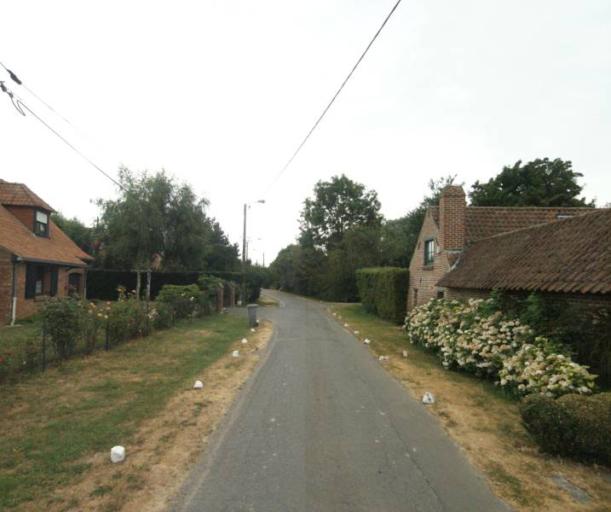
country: FR
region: Nord-Pas-de-Calais
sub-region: Departement du Nord
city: Bondues
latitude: 50.7005
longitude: 3.1049
